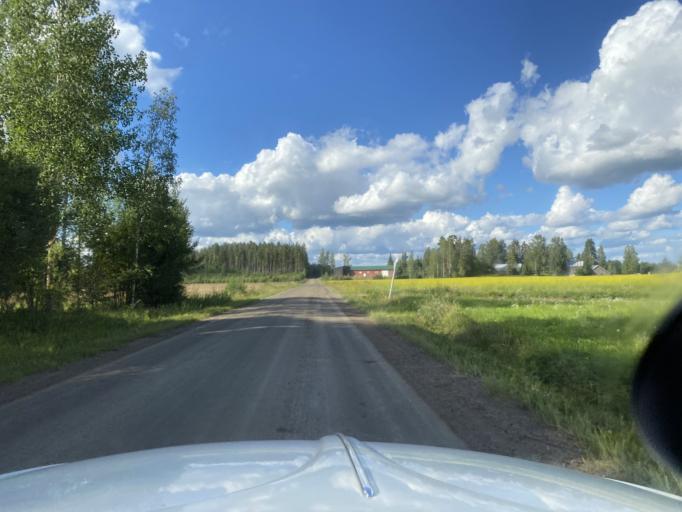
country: FI
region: Pirkanmaa
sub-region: Lounais-Pirkanmaa
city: Punkalaidun
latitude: 61.1127
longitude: 23.2742
